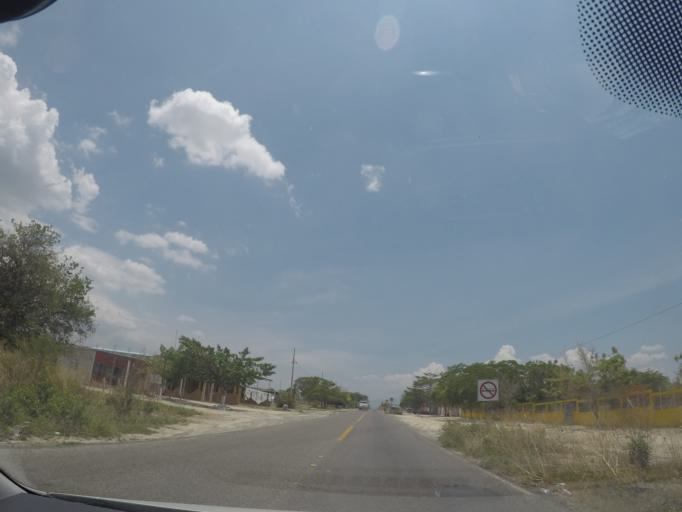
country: MX
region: Oaxaca
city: Santa Maria Jalapa del Marques
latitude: 16.4398
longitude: -95.4645
